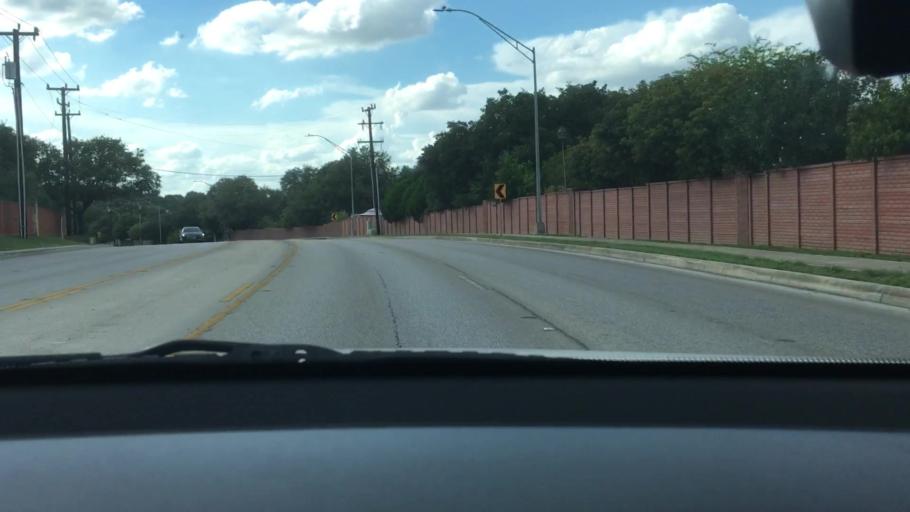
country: US
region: Texas
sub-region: Bexar County
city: Live Oak
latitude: 29.5922
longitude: -98.3978
